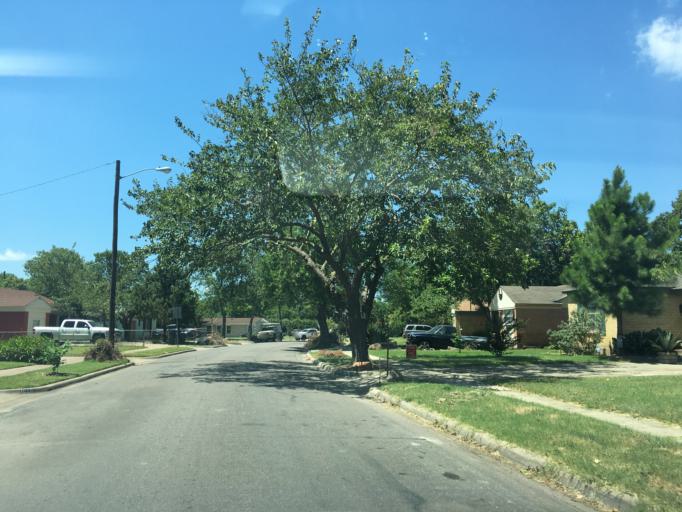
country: US
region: Texas
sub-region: Dallas County
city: Garland
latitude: 32.8380
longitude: -96.6802
